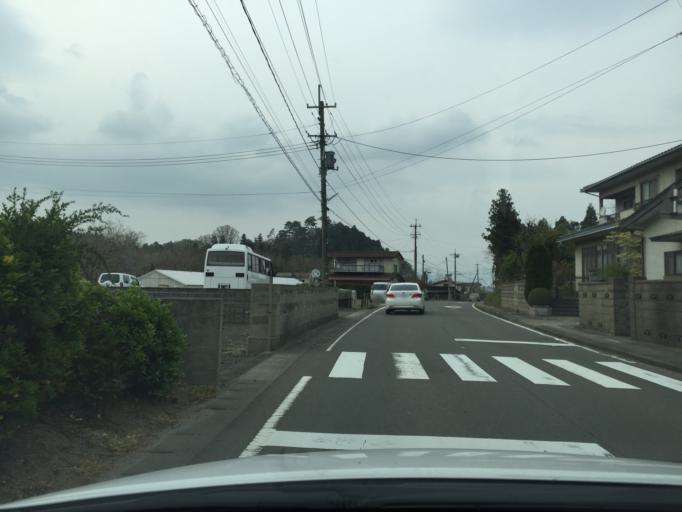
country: JP
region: Fukushima
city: Fukushima-shi
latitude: 37.7191
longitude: 140.4739
